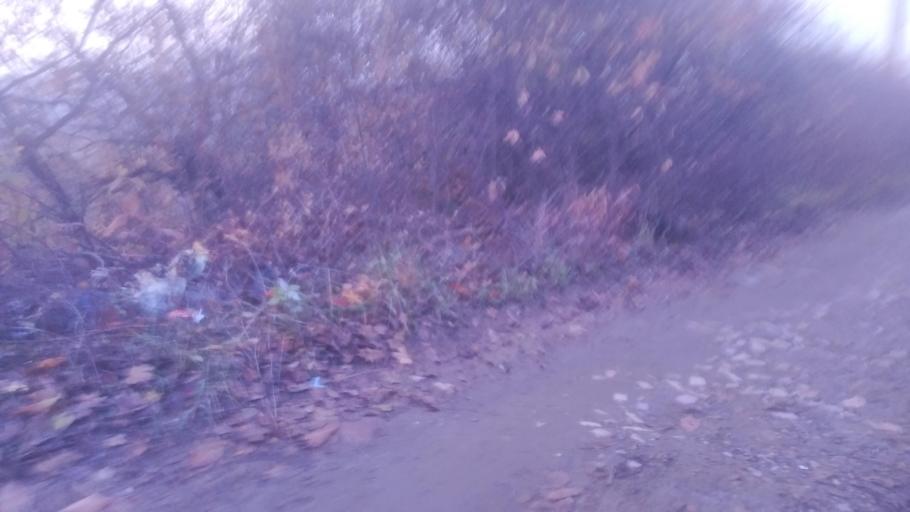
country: HU
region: Pest
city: Urom
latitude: 47.6078
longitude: 19.0286
